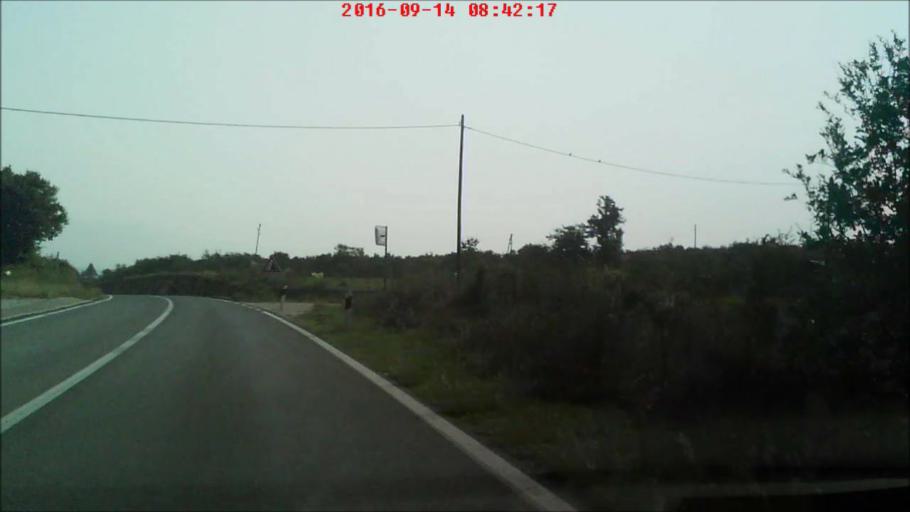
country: HR
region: Zadarska
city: Policnik
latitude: 44.1892
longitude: 15.4031
